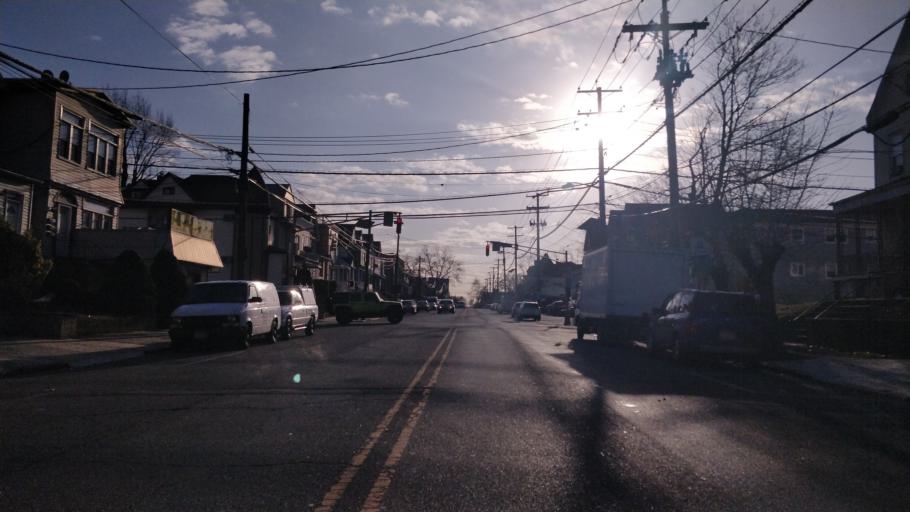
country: US
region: New Jersey
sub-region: Hudson County
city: Bayonne
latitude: 40.6703
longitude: -74.1097
